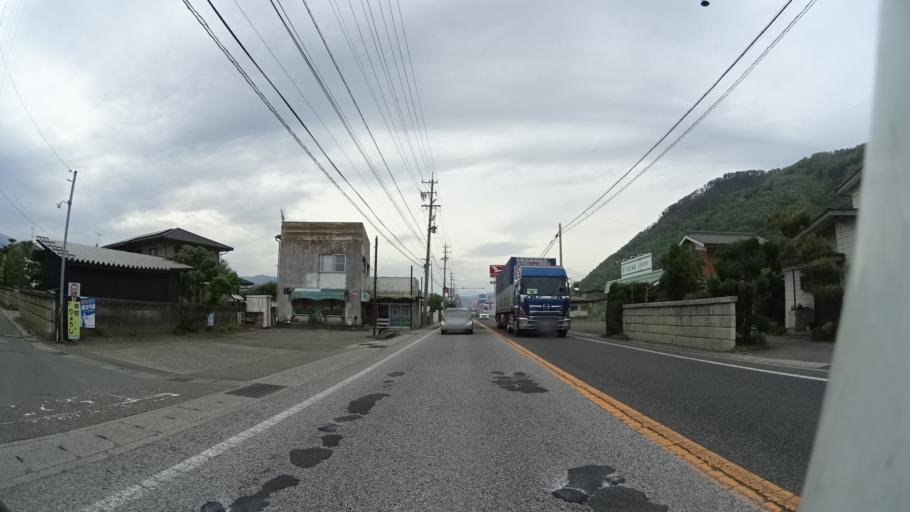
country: JP
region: Nagano
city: Nagano-shi
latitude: 36.5086
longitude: 138.1391
